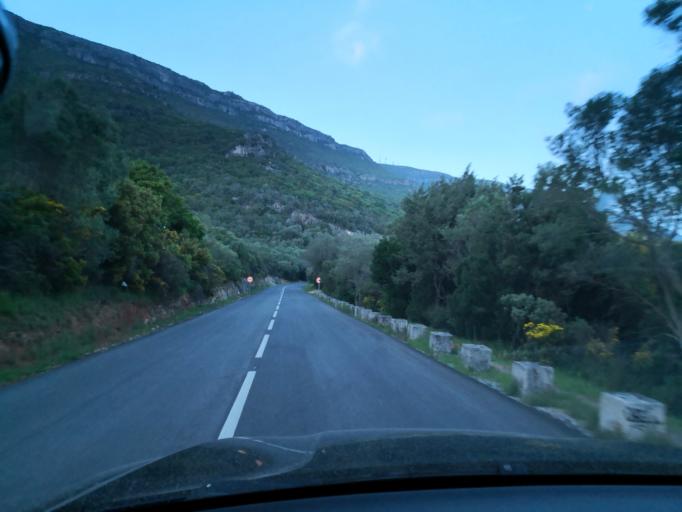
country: PT
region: Setubal
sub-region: Palmela
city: Quinta do Anjo
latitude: 38.4829
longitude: -8.9793
